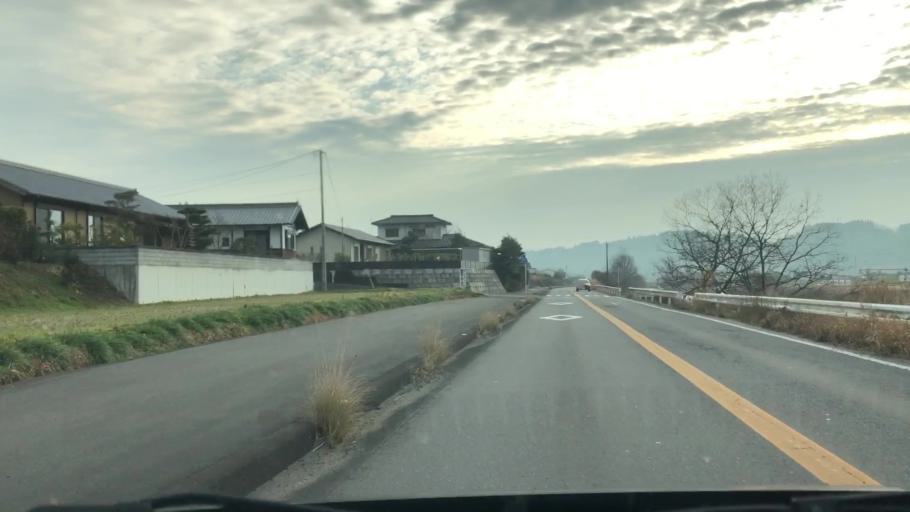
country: JP
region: Oita
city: Takedamachi
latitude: 32.9684
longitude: 131.4761
